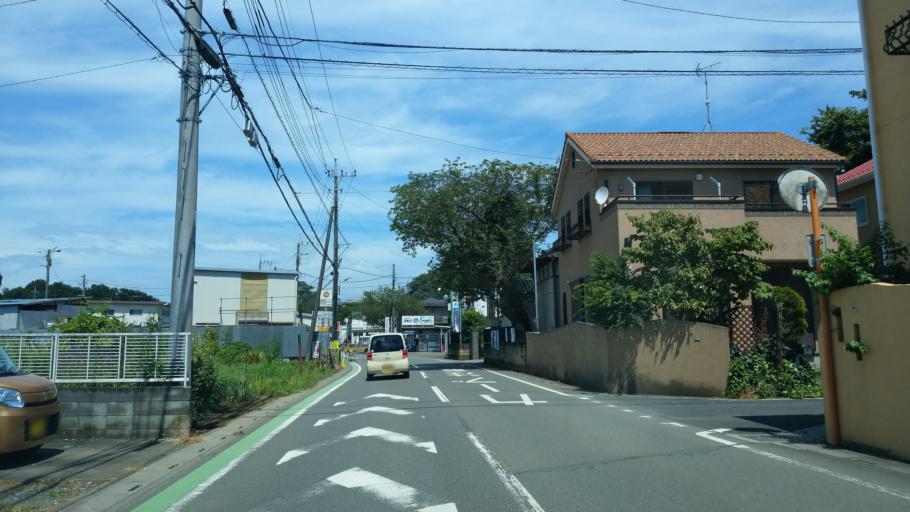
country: JP
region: Saitama
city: Ageoshimo
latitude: 35.9291
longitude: 139.5649
